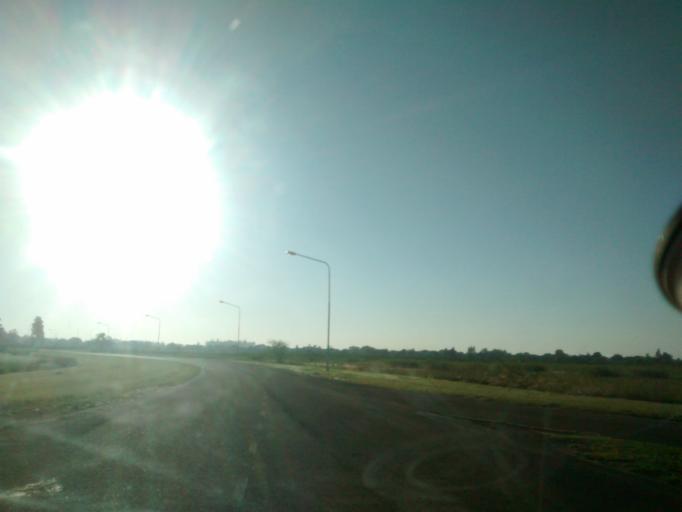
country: AR
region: Chaco
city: Fontana
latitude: -27.4448
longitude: -59.0467
